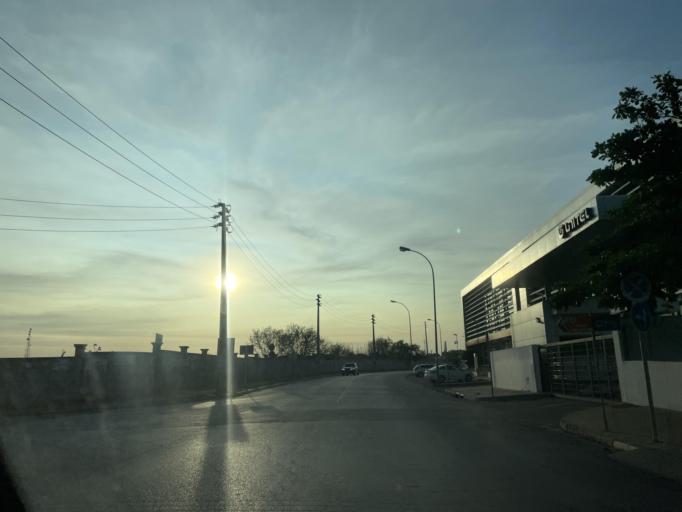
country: AO
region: Luanda
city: Luanda
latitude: -8.9310
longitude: 13.1892
